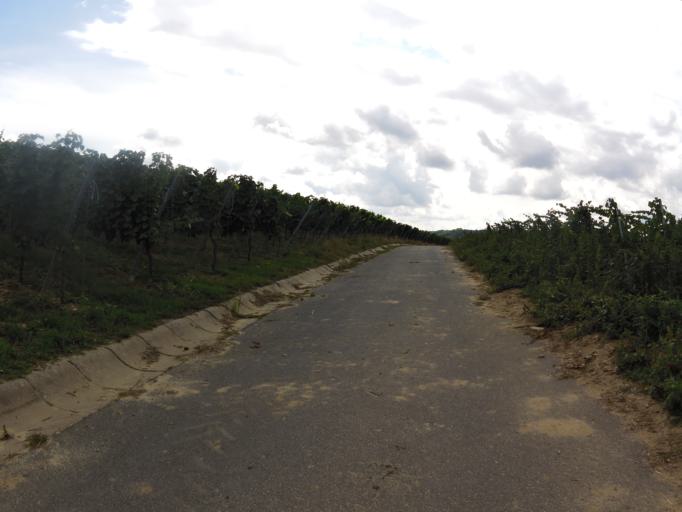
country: DE
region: Bavaria
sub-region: Regierungsbezirk Unterfranken
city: Sommerhausen
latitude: 49.6926
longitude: 10.0301
